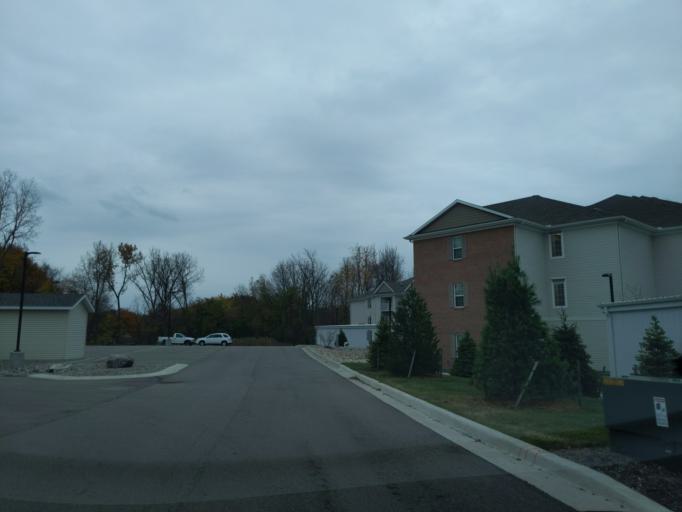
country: US
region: Michigan
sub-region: Ingham County
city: Edgemont Park
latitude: 42.7087
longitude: -84.5929
